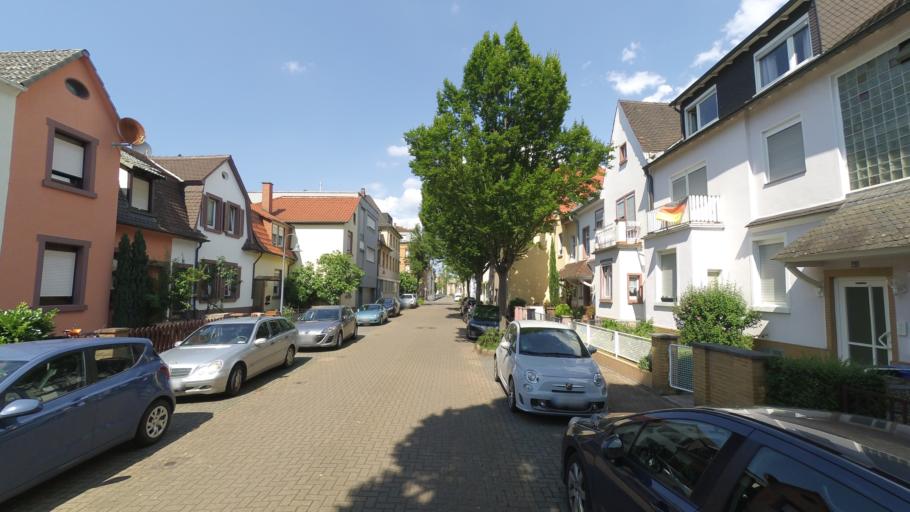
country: DE
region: Rheinland-Pfalz
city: Ludwigshafen am Rhein
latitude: 49.4941
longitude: 8.4161
